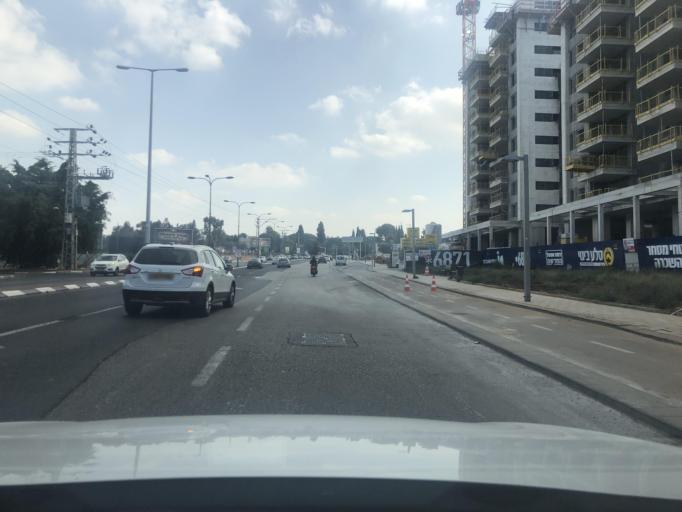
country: IL
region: Tel Aviv
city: Giv`at Shemu'el
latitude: 32.0514
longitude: 34.8393
